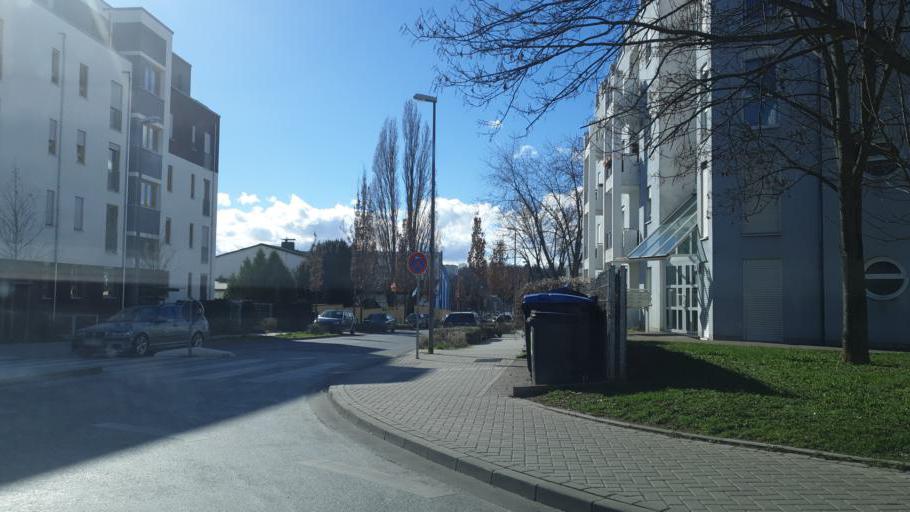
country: DE
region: Hesse
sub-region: Regierungsbezirk Darmstadt
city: Wiesbaden
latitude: 50.0631
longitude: 8.2574
